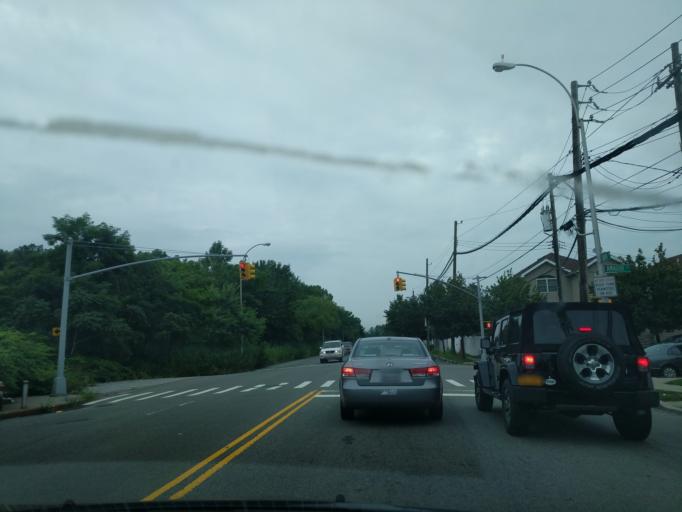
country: US
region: New York
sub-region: Richmond County
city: Bloomfield
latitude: 40.6237
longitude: -74.1675
